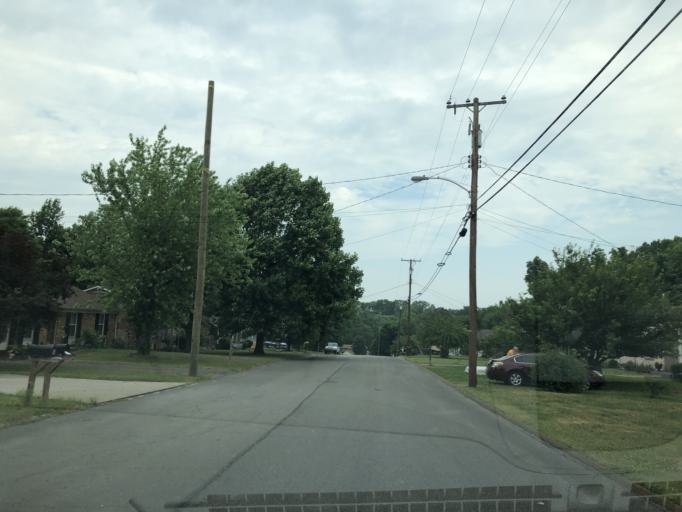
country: US
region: Tennessee
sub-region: Davidson County
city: Oak Hill
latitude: 36.0738
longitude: -86.6873
